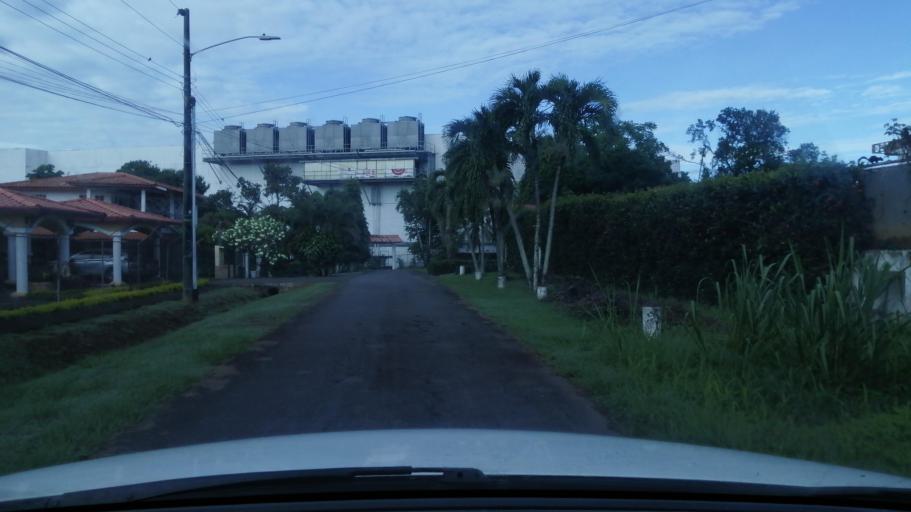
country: PA
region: Chiriqui
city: Mata del Nance
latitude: 8.4468
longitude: -82.4188
